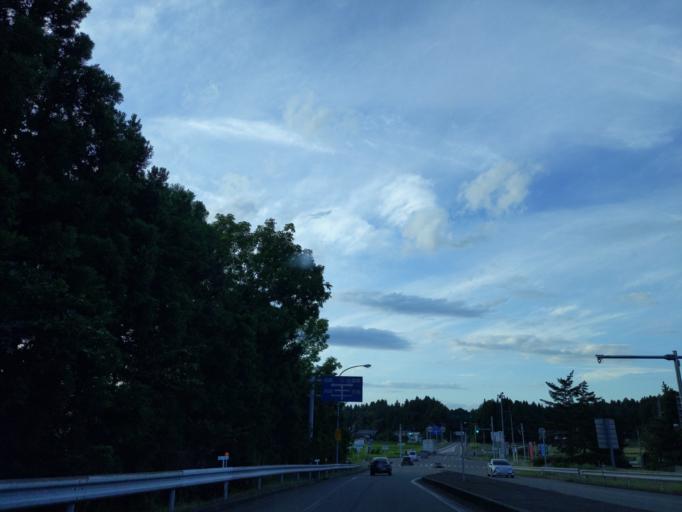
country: JP
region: Niigata
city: Kashiwazaki
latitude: 37.4434
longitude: 138.6561
